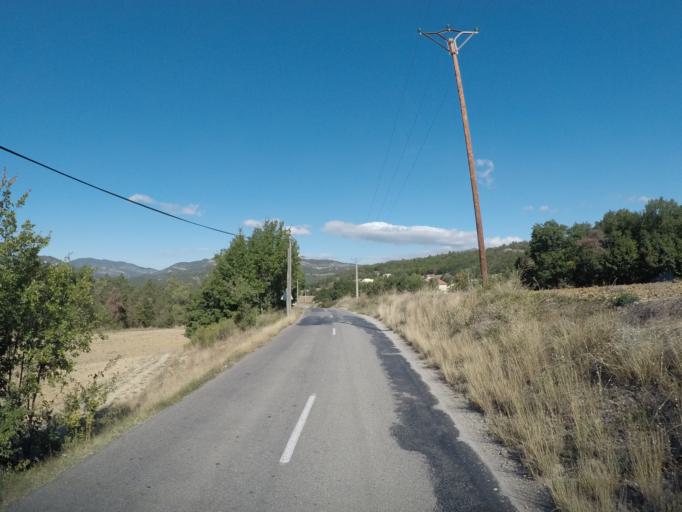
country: FR
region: Provence-Alpes-Cote d'Azur
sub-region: Departement des Alpes-de-Haute-Provence
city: Mallemoisson
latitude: 44.0422
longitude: 6.1683
